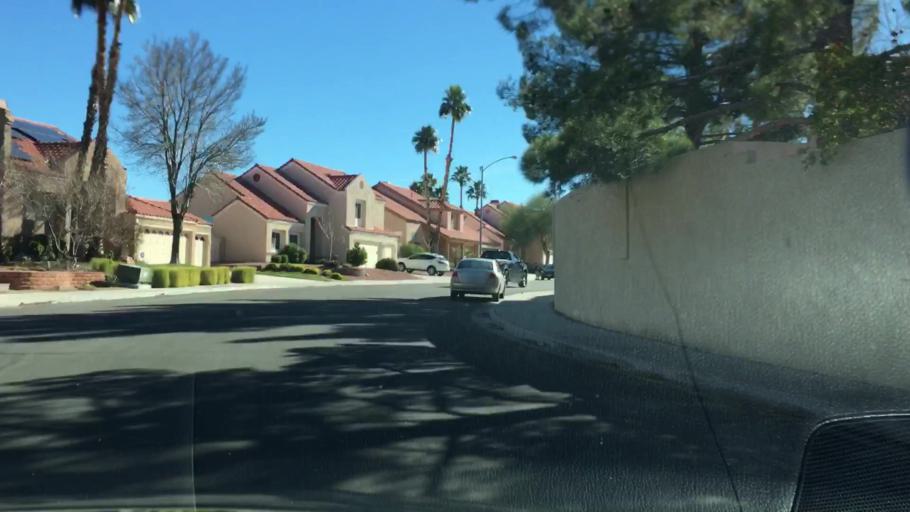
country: US
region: Nevada
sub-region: Clark County
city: Whitney
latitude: 36.0600
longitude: -115.0629
